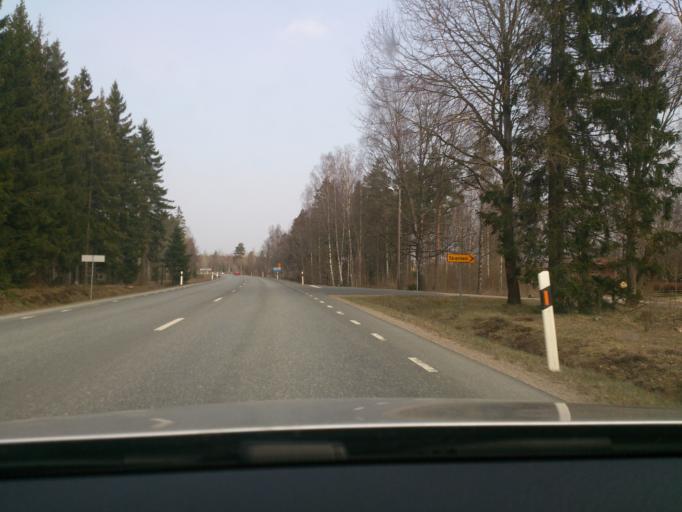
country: SE
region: Kronoberg
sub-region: Alvesta Kommun
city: Moheda
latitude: 56.9815
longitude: 14.5676
